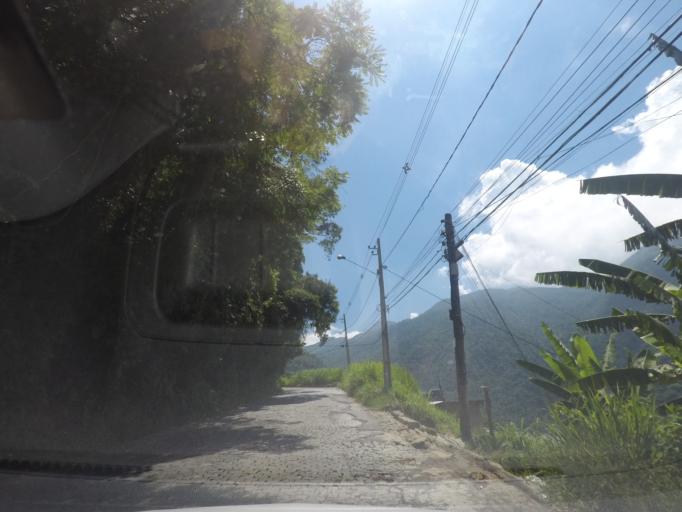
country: BR
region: Rio de Janeiro
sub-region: Petropolis
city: Petropolis
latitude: -22.5379
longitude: -43.1763
